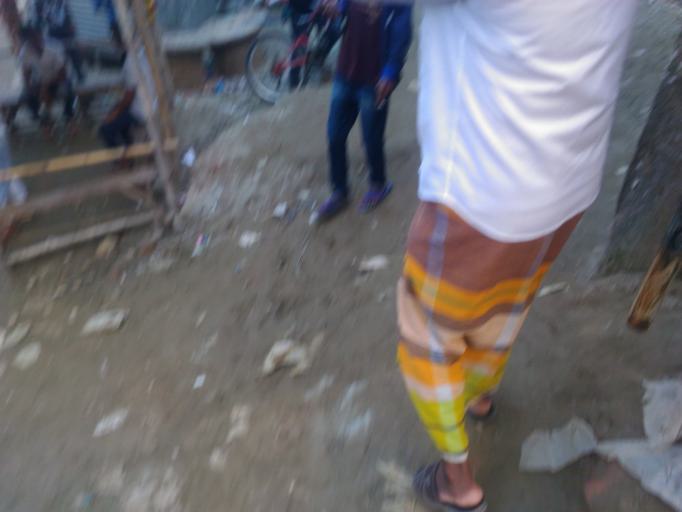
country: BD
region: Dhaka
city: Tungi
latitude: 23.8407
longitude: 90.3660
